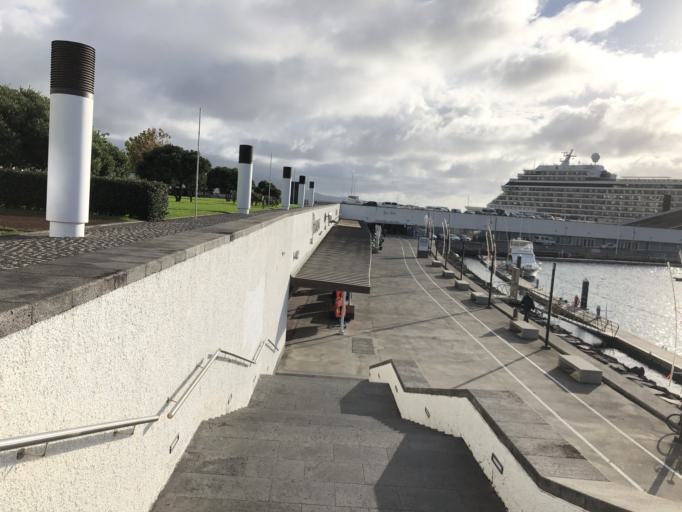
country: PT
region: Azores
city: Ponta Delgada
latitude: 37.7397
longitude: -25.6645
